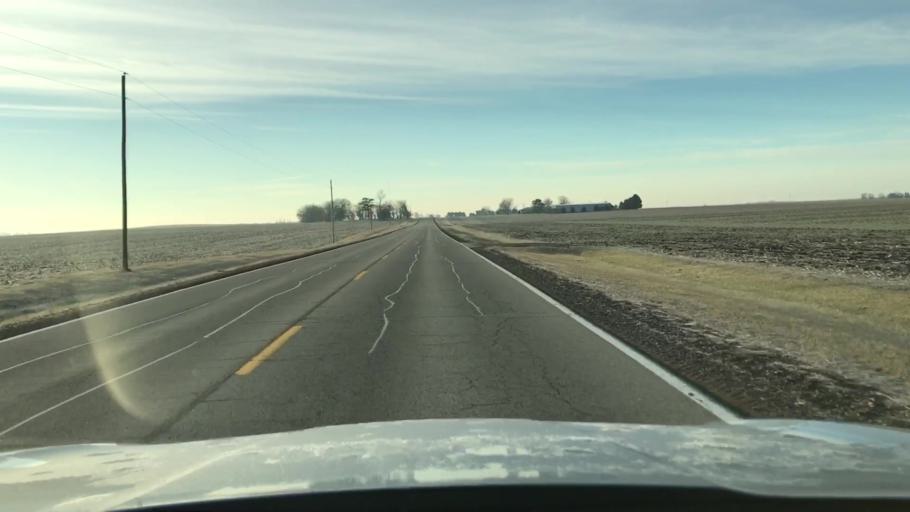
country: US
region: Illinois
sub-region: McLean County
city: Hudson
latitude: 40.5974
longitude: -88.9449
